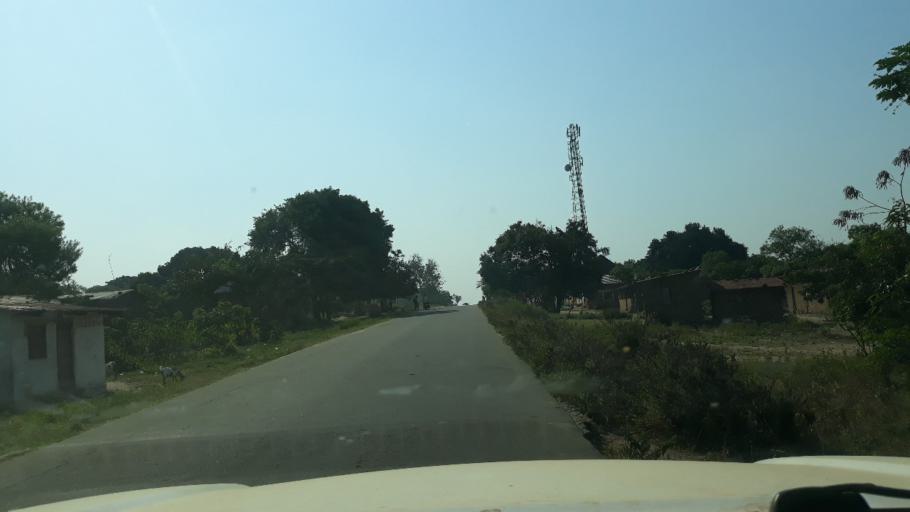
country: BI
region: Cibitoke
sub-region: Commune of Buganda
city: Buganda
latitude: -2.9962
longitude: 29.0956
